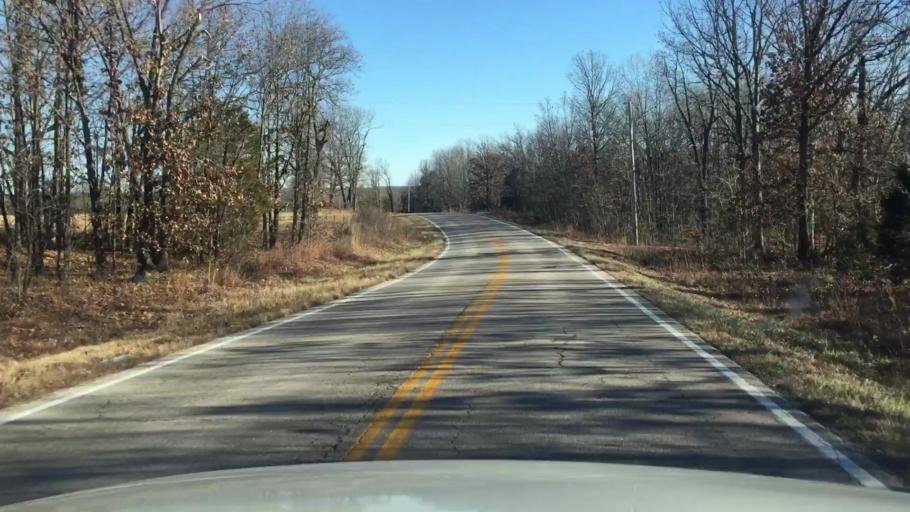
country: US
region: Missouri
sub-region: Morgan County
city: Versailles
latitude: 38.3463
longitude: -92.7408
